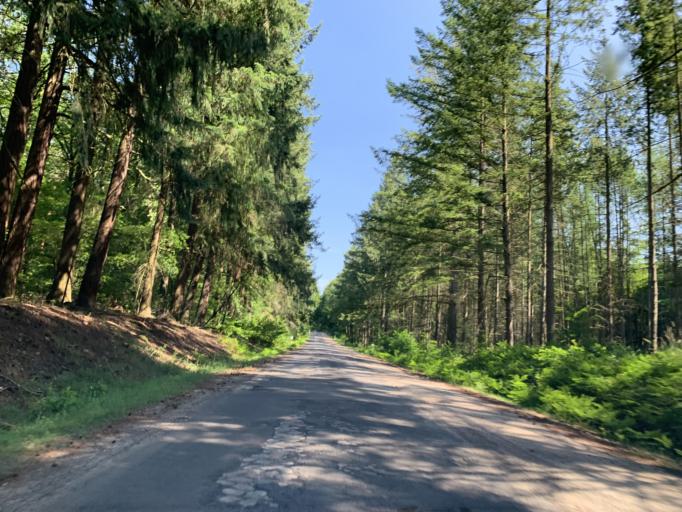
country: DE
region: Mecklenburg-Vorpommern
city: Carpin
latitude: 53.3174
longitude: 13.2859
